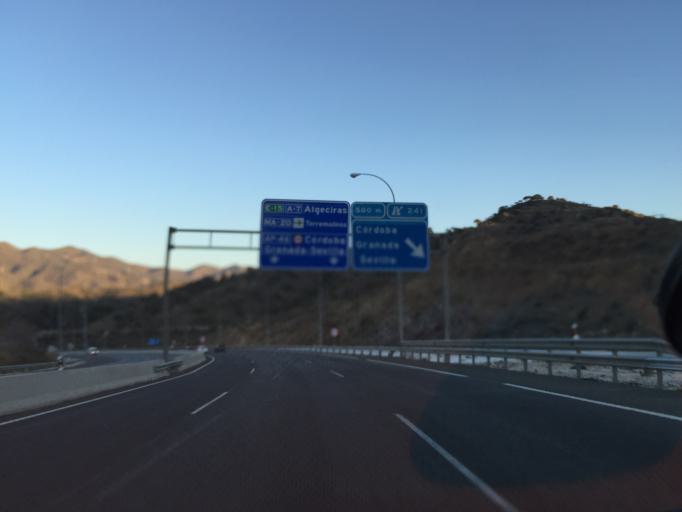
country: ES
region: Andalusia
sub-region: Provincia de Malaga
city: Malaga
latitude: 36.7543
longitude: -4.4159
